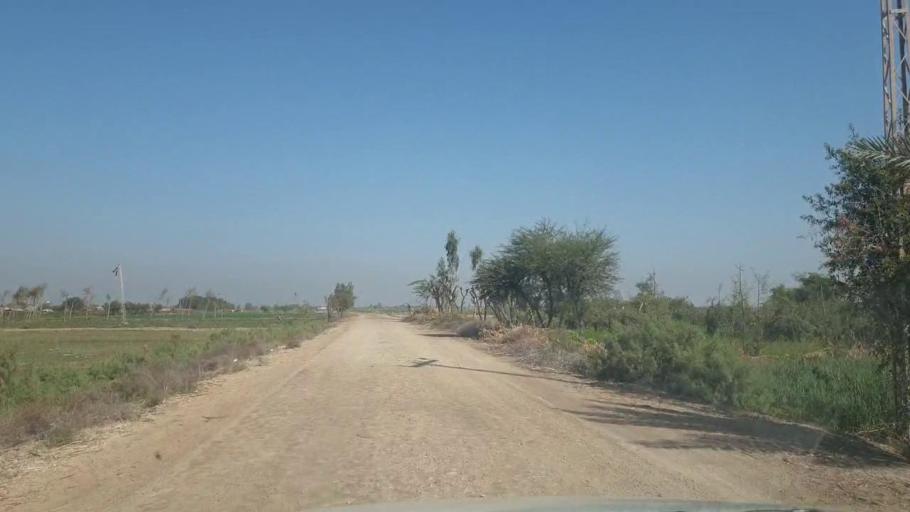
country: PK
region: Sindh
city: Mirpur Khas
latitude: 25.5017
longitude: 69.1483
